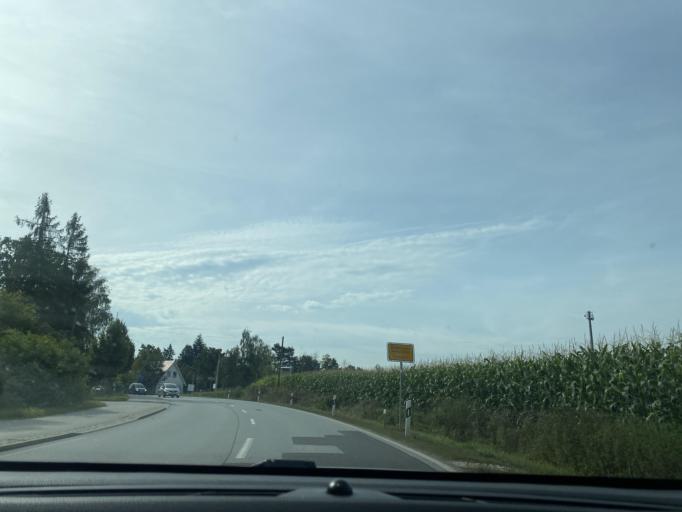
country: DE
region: Saxony
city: Reichenbach
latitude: 51.1964
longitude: 14.7559
